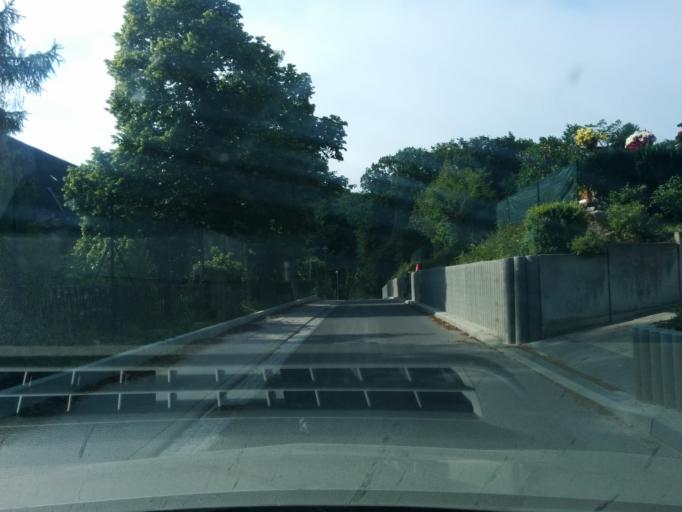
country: DE
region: Mecklenburg-Vorpommern
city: Ostseebad Zinnowitz
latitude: 54.0736
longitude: 13.9184
